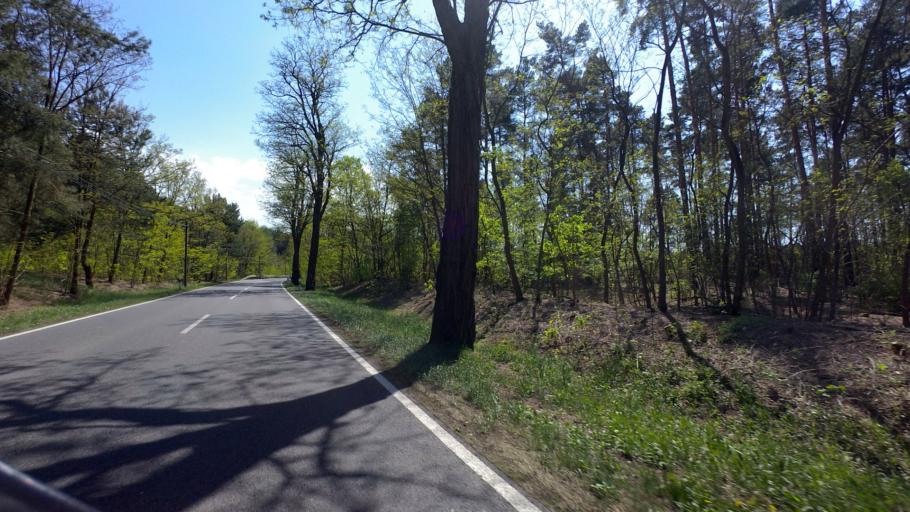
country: DE
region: Brandenburg
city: Lieberose
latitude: 51.9974
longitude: 14.2029
